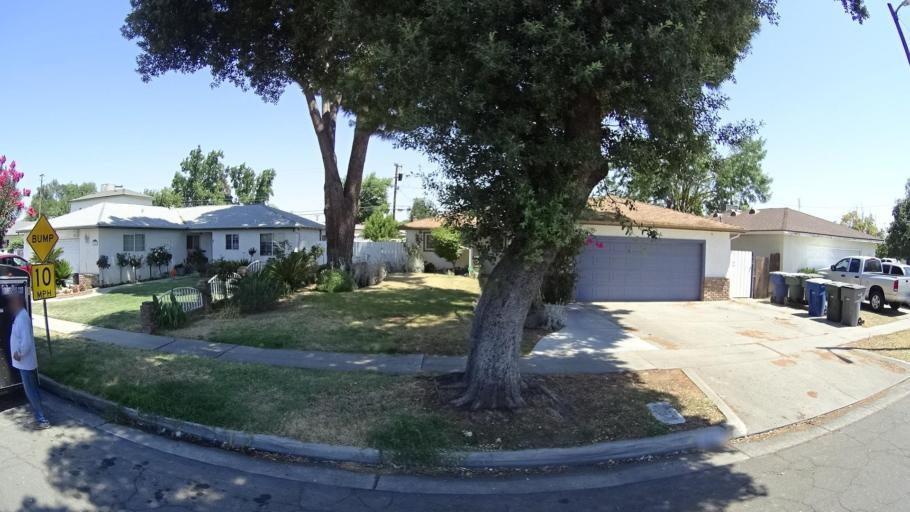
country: US
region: California
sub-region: Fresno County
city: Fresno
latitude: 36.7981
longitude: -119.7602
